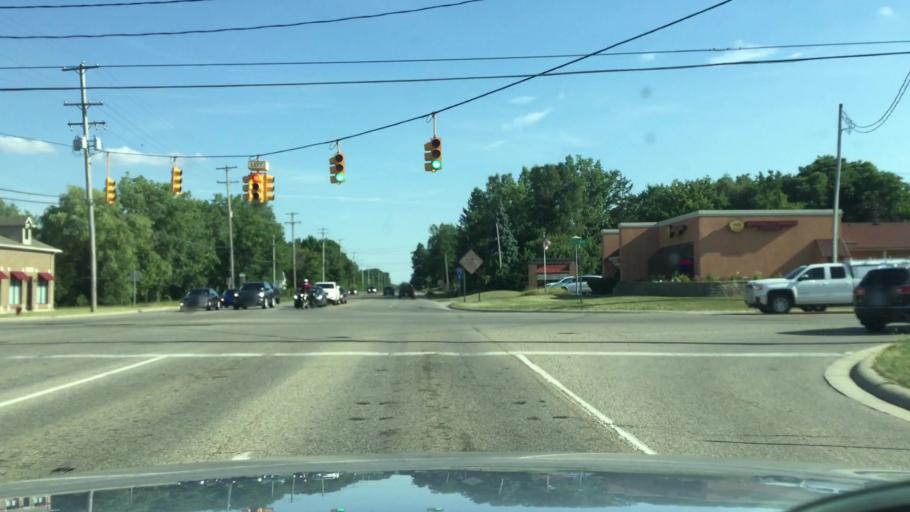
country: US
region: Michigan
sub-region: Genesee County
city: Grand Blanc
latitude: 42.8875
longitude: -83.5992
